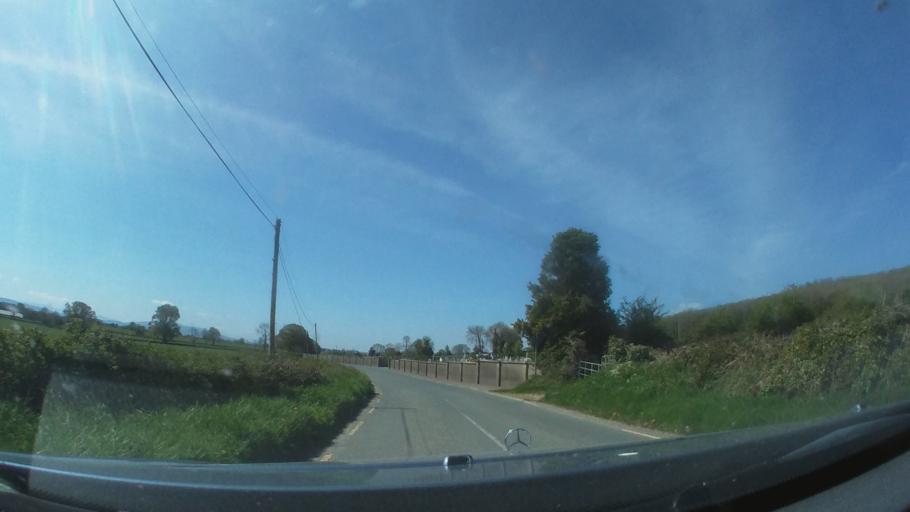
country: IE
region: Leinster
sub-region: Kilkenny
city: Callan
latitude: 52.6093
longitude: -7.3834
